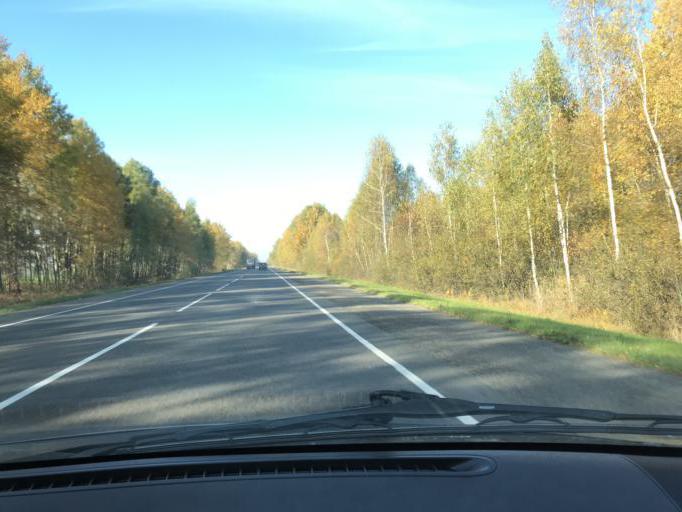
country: BY
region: Brest
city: Horad Luninyets
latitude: 52.2969
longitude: 26.7420
